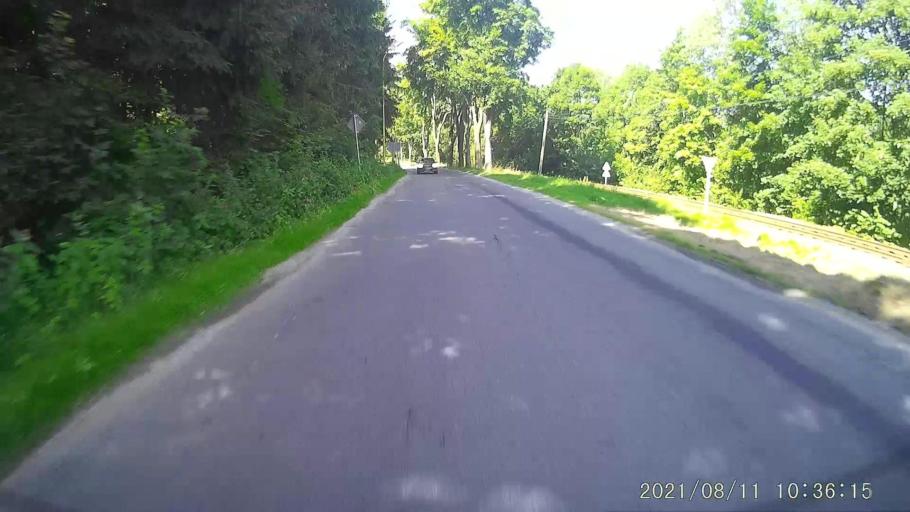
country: PL
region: Lower Silesian Voivodeship
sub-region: Powiat klodzki
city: Szczytna
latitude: 50.4027
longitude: 16.4629
